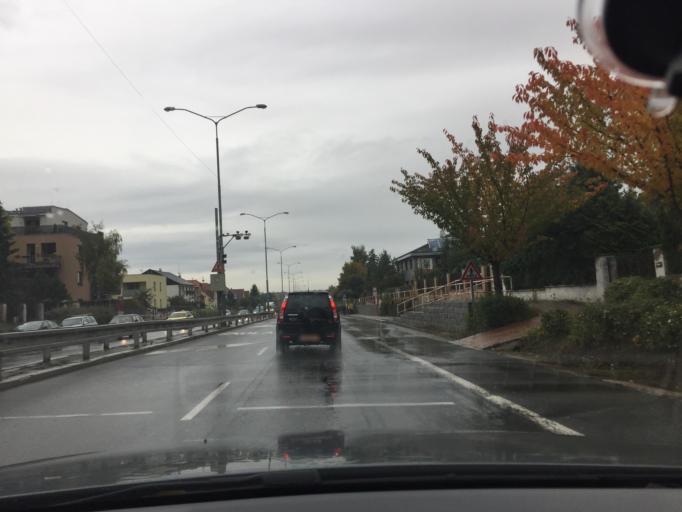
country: CZ
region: Central Bohemia
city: Zdiby
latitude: 50.1433
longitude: 14.4511
